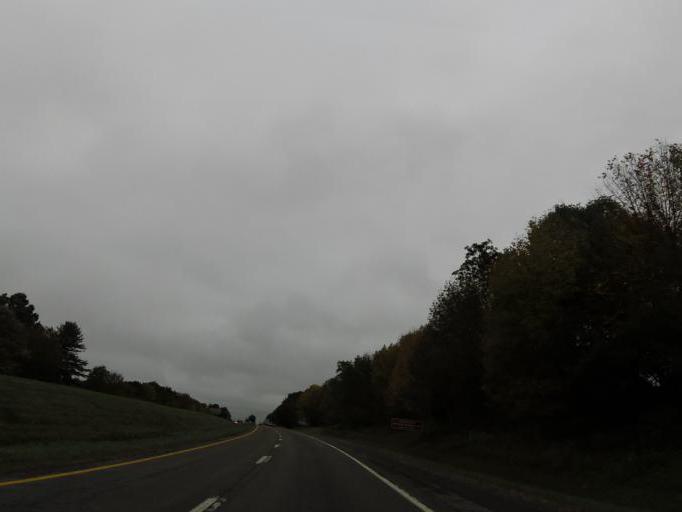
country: US
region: Virginia
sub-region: Wythe County
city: Wytheville
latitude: 36.9658
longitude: -81.0799
